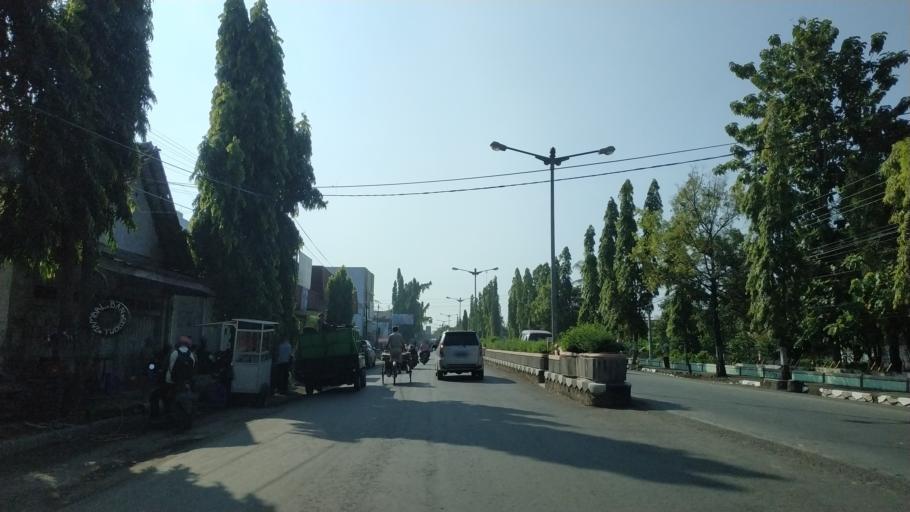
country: ID
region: Central Java
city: Pemalang
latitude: -6.8912
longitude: 109.3962
